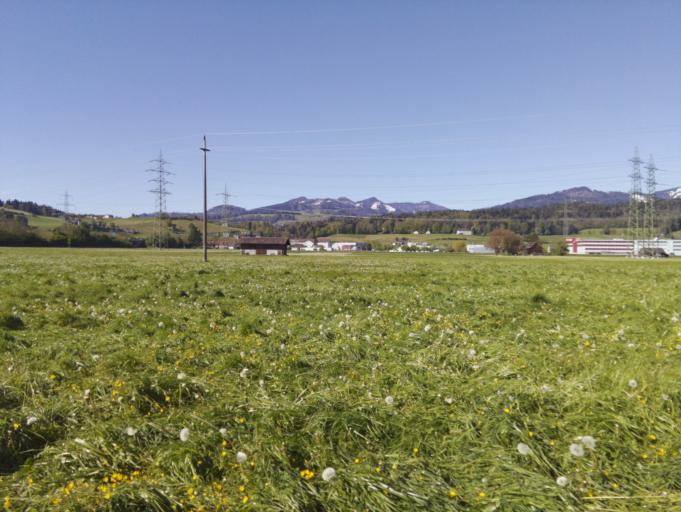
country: CH
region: Saint Gallen
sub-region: Wahlkreis See-Gaster
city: Uznach
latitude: 47.2201
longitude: 8.9664
